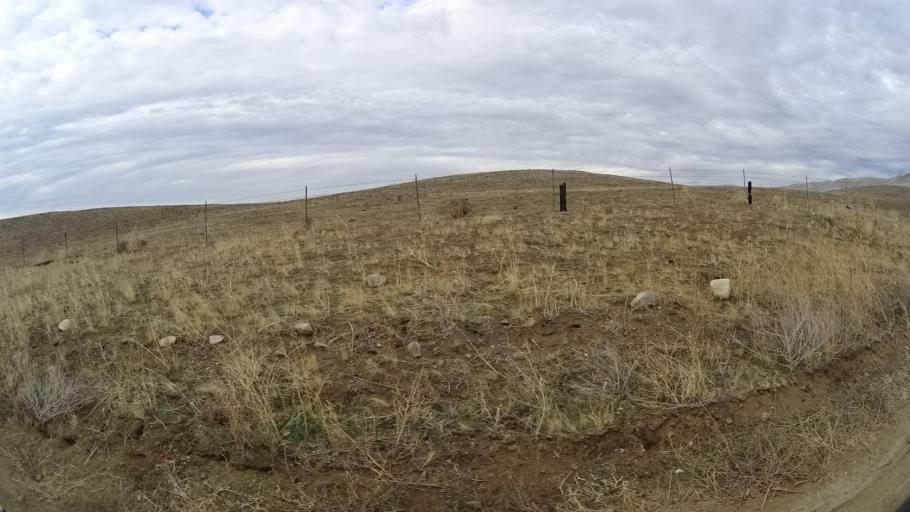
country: US
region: California
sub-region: Kern County
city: Arvin
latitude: 35.1378
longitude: -118.7928
